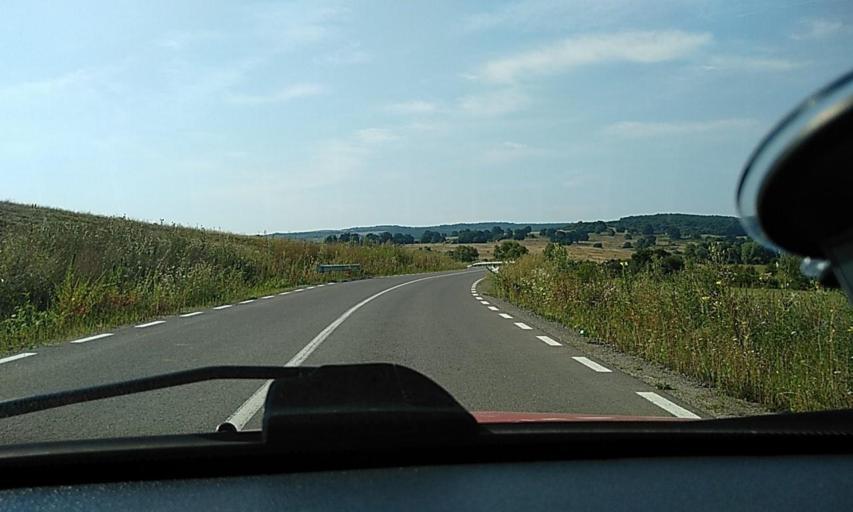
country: RO
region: Brasov
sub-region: Comuna Bunesti
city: Bunesti
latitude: 46.0780
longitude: 25.0660
